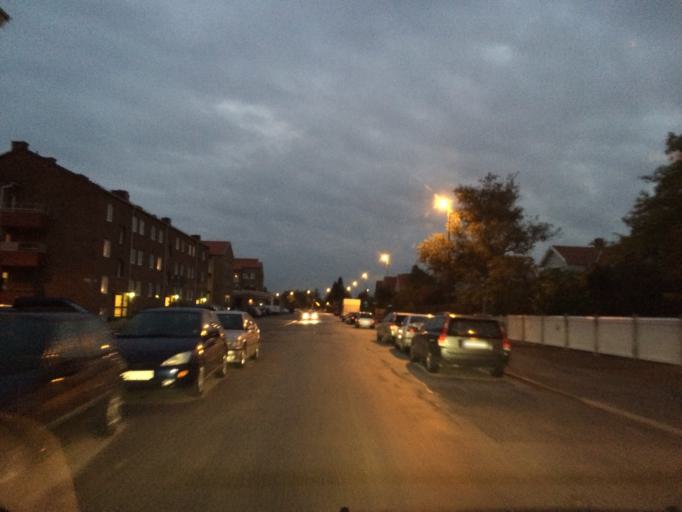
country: SE
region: Skane
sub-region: Malmo
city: Bunkeflostrand
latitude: 55.5814
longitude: 12.9428
